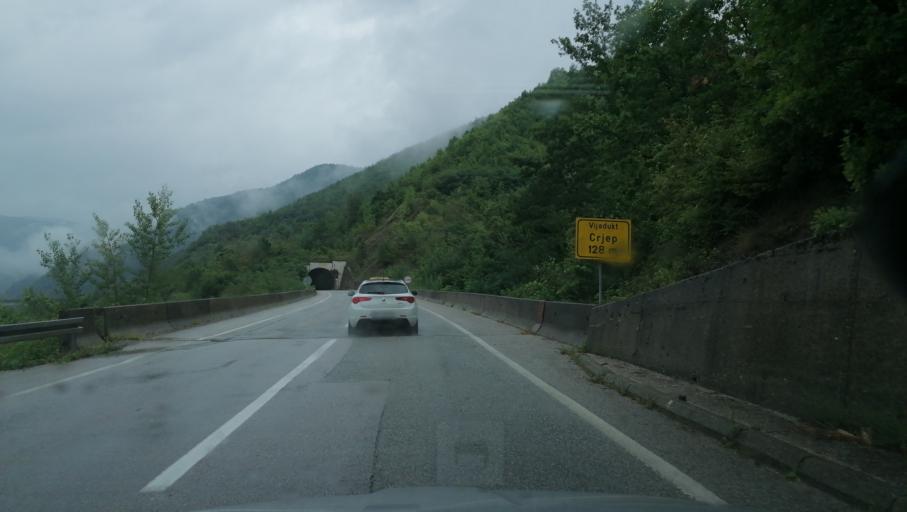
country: BA
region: Republika Srpska
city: Visegrad
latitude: 43.7278
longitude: 19.1694
